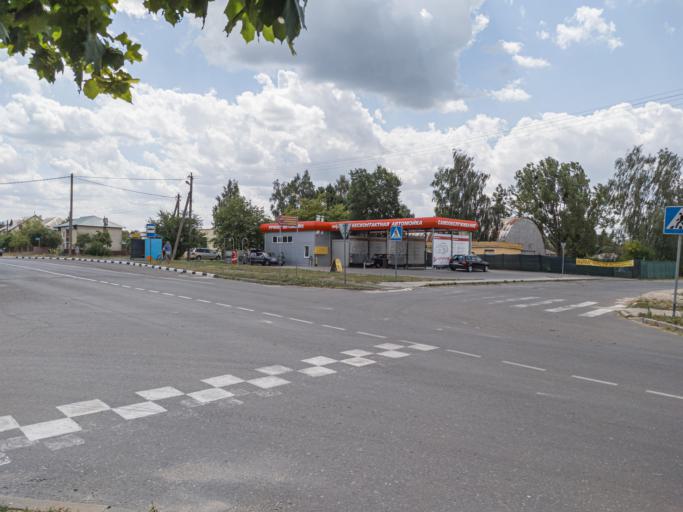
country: BY
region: Brest
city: Kamyanyets
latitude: 52.3941
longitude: 23.8326
